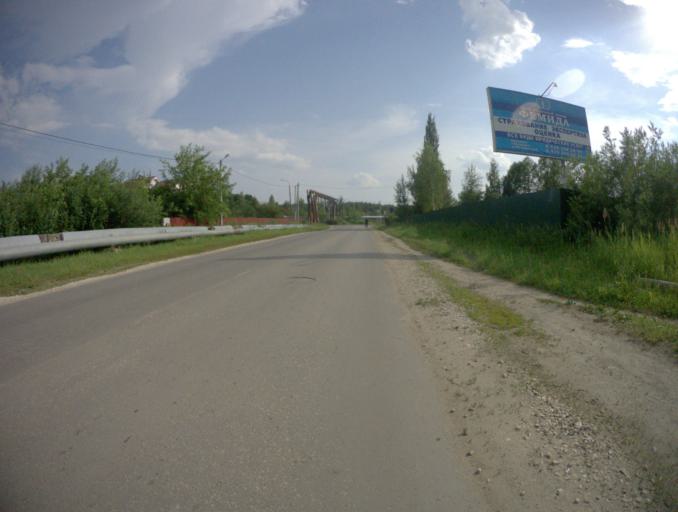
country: RU
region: Nizjnij Novgorod
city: Mulino
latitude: 56.2282
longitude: 42.9472
